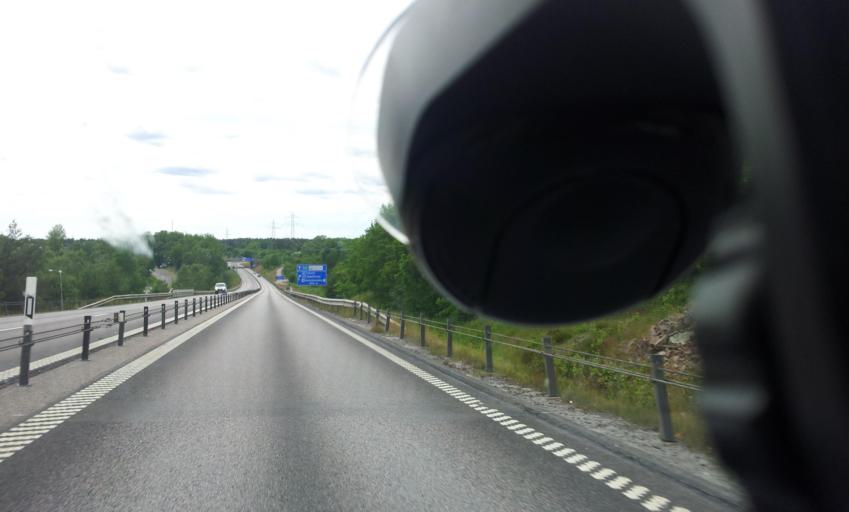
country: SE
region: Kalmar
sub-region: Oskarshamns Kommun
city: Oskarshamn
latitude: 57.2696
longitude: 16.4358
